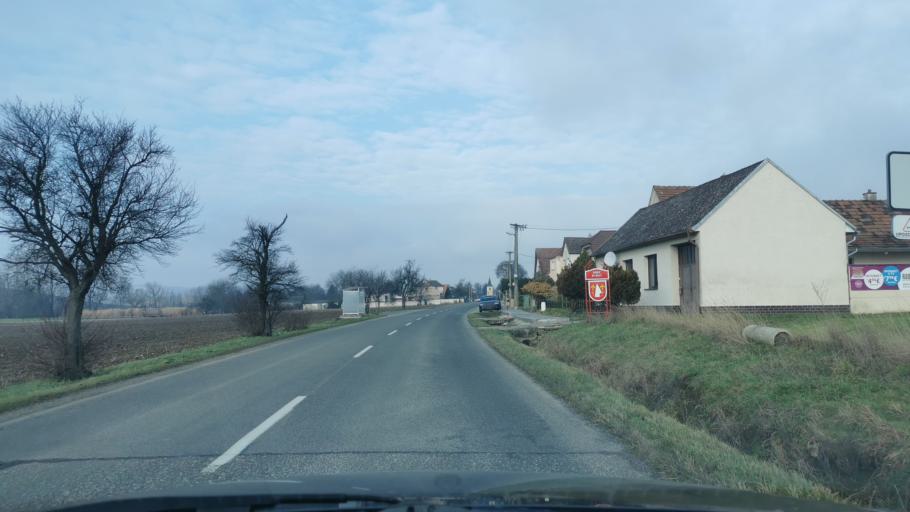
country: SK
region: Trnavsky
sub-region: Okres Senica
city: Senica
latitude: 48.7021
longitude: 17.3434
